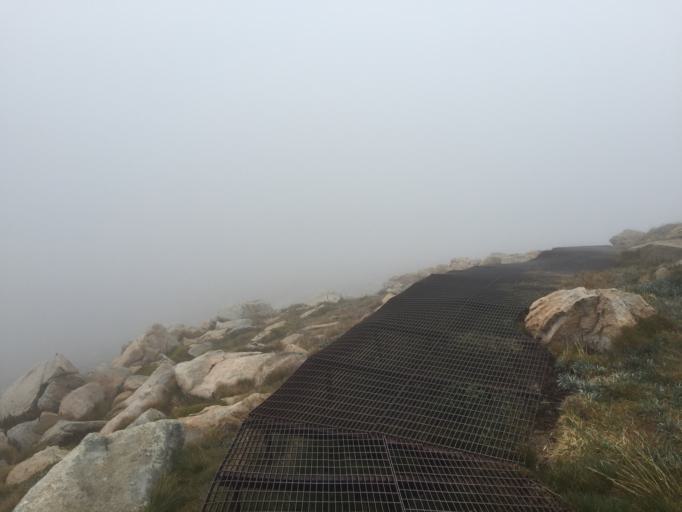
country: AU
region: New South Wales
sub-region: Snowy River
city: Jindabyne
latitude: -36.4659
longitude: 148.2699
